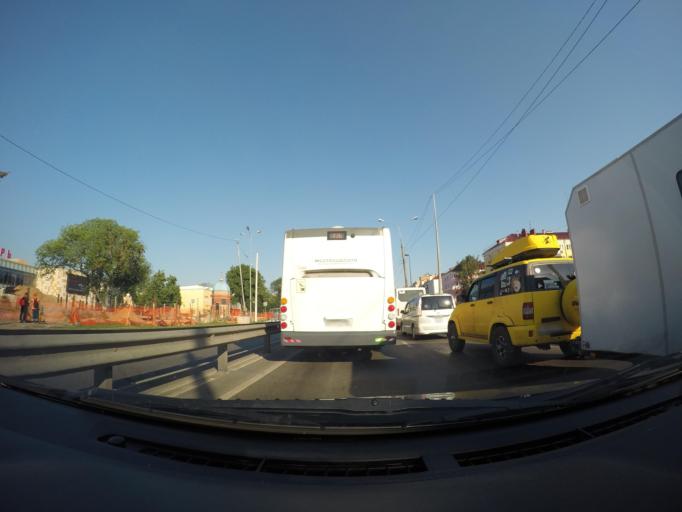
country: RU
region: Moskovskaya
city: Lyubertsy
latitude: 55.6776
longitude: 37.8969
